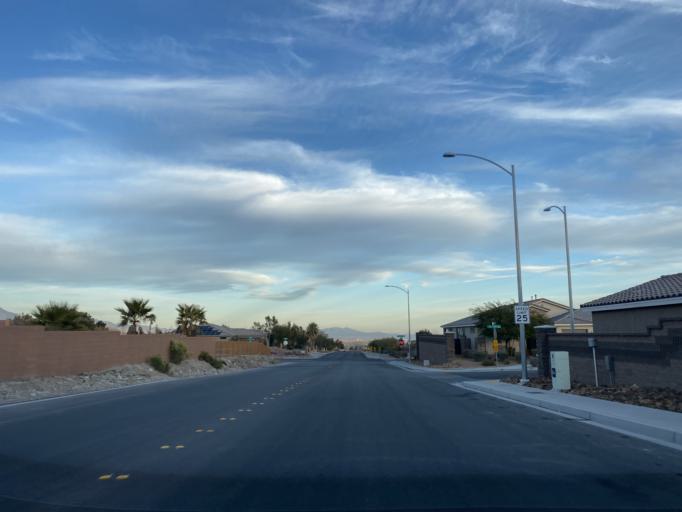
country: US
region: Nevada
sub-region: Clark County
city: Summerlin South
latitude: 36.2884
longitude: -115.3136
